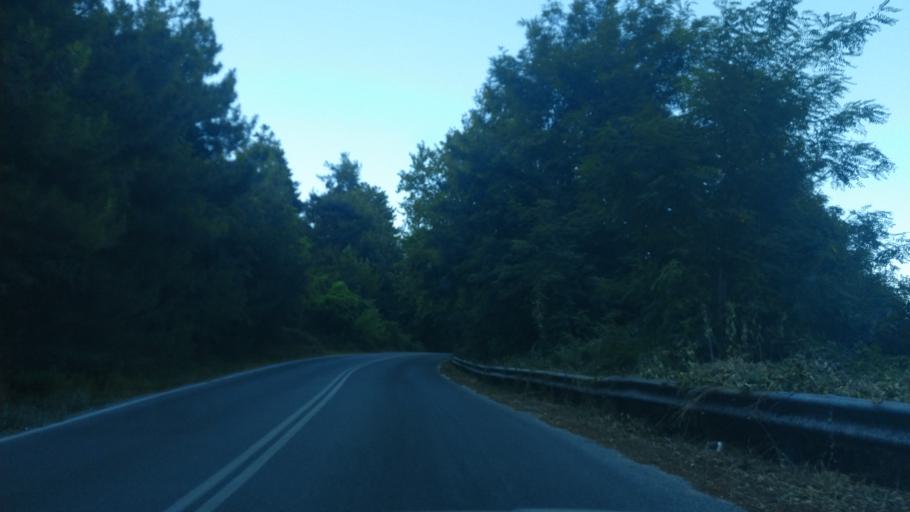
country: GR
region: East Macedonia and Thrace
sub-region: Nomos Kavalas
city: Potamia
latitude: 40.7200
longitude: 24.7333
